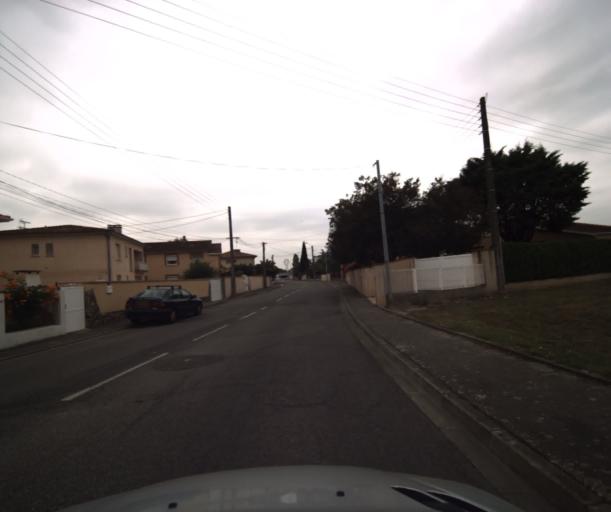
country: FR
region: Midi-Pyrenees
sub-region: Departement de la Haute-Garonne
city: Portet-sur-Garonne
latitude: 43.5197
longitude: 1.4001
